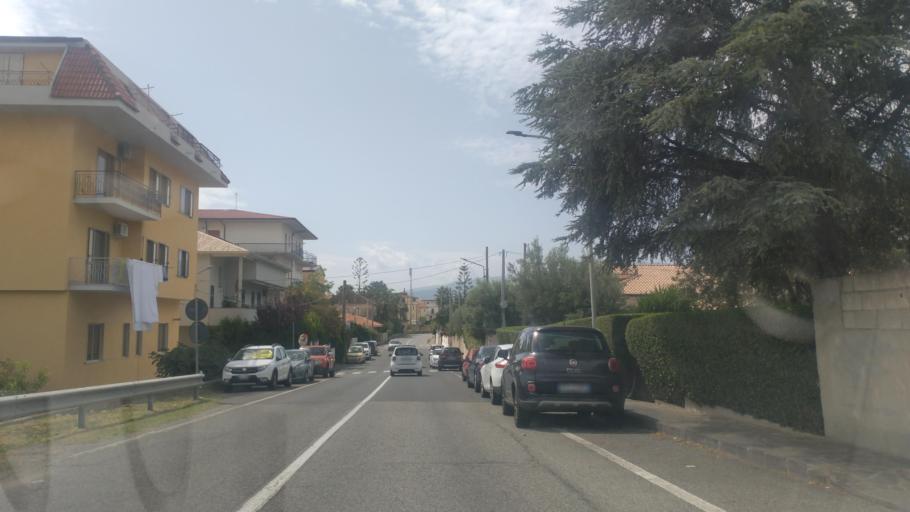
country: IT
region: Calabria
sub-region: Provincia di Catanzaro
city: Montepaone Lido
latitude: 38.7327
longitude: 16.5446
